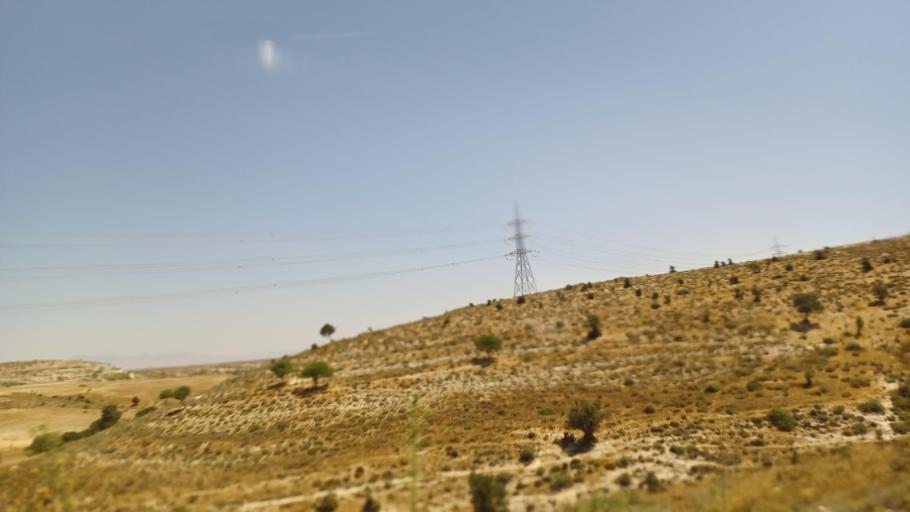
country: CY
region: Lefkosia
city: Lympia
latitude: 34.9846
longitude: 33.4801
